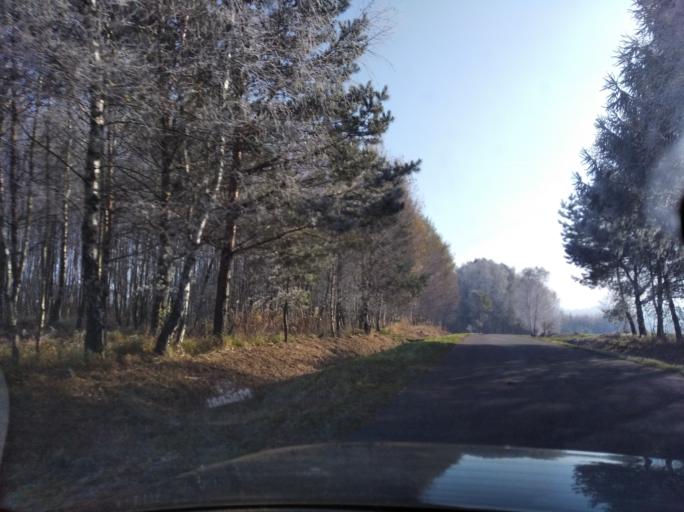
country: PL
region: Subcarpathian Voivodeship
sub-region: Powiat strzyzowski
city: Wysoka Strzyzowska
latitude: 49.8386
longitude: 21.7113
